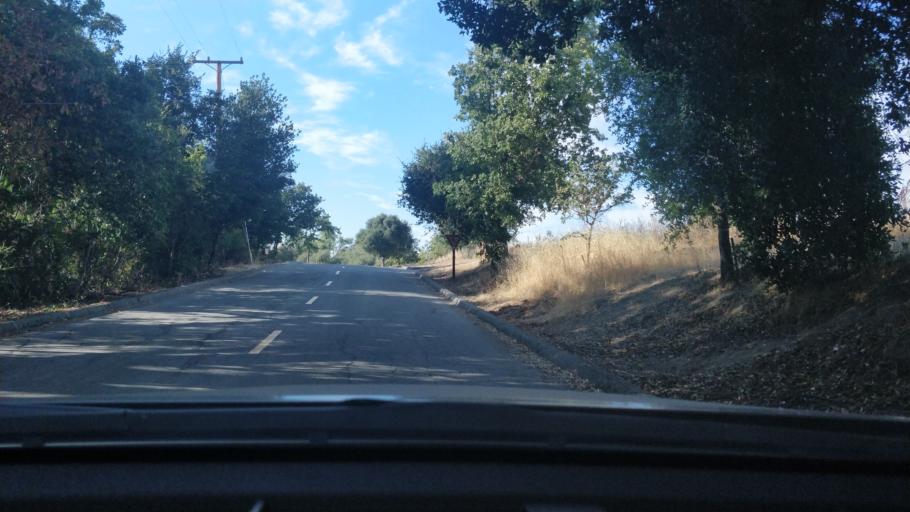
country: US
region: California
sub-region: Santa Clara County
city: East Foothills
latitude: 37.3393
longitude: -121.7198
